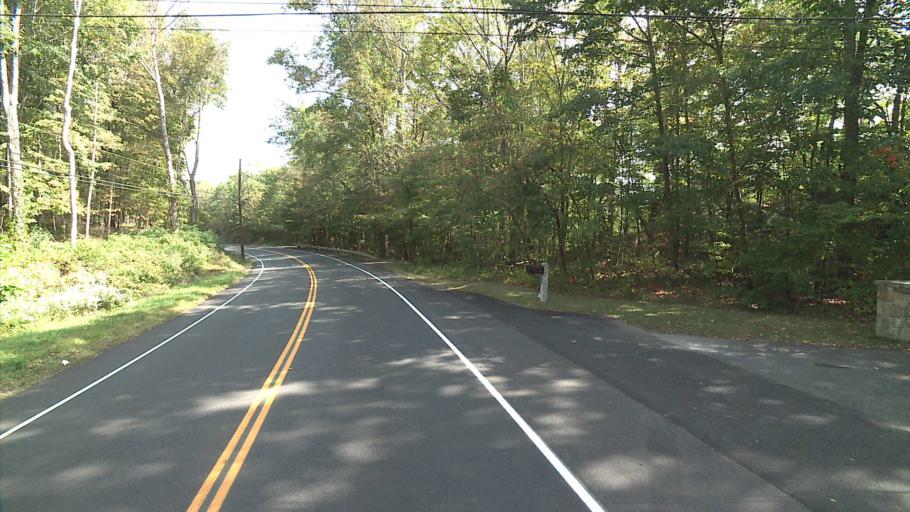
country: US
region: Connecticut
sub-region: New Haven County
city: Southbury
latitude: 41.3853
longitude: -73.2033
